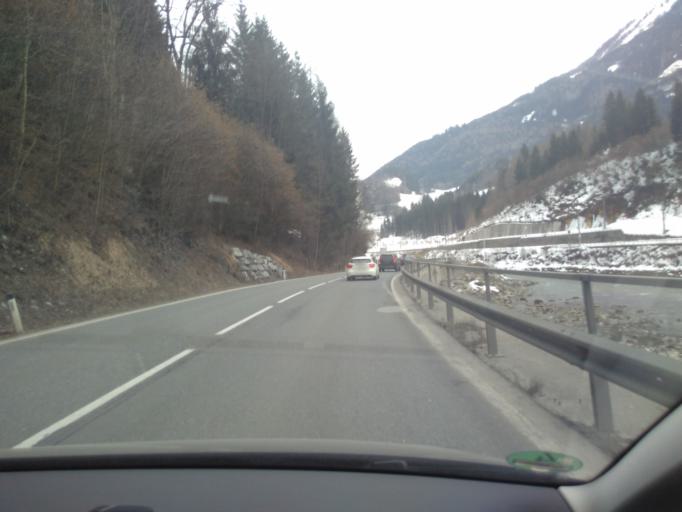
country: AT
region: Salzburg
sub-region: Politischer Bezirk Sankt Johann im Pongau
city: Goldegg
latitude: 47.3104
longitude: 13.1189
